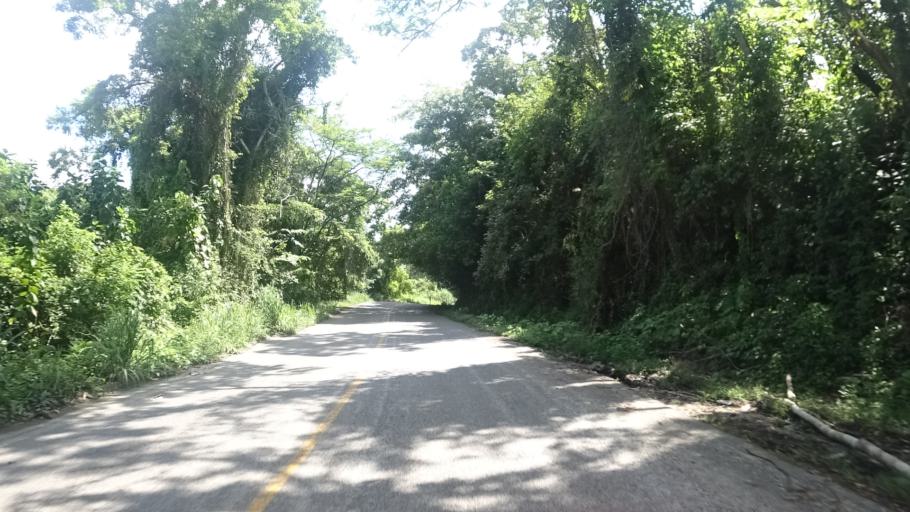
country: MX
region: Chiapas
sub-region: Salto de Agua
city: Belisario Dominguez
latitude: 17.4435
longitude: -91.9749
